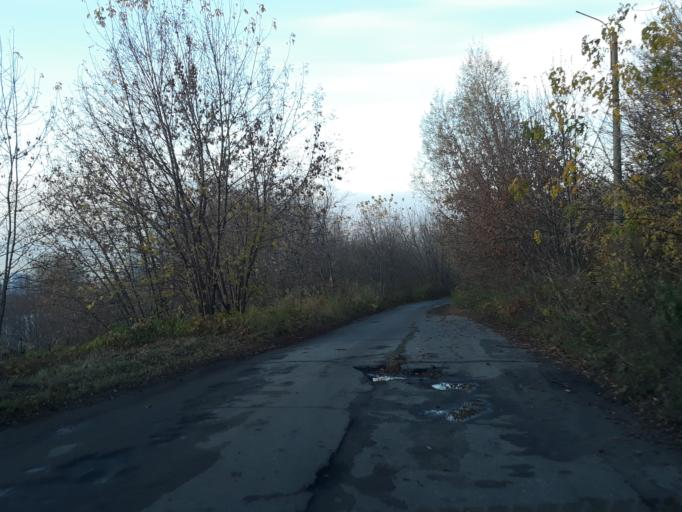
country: RU
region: Nizjnij Novgorod
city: Nizhniy Novgorod
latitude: 56.2833
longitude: 43.9697
